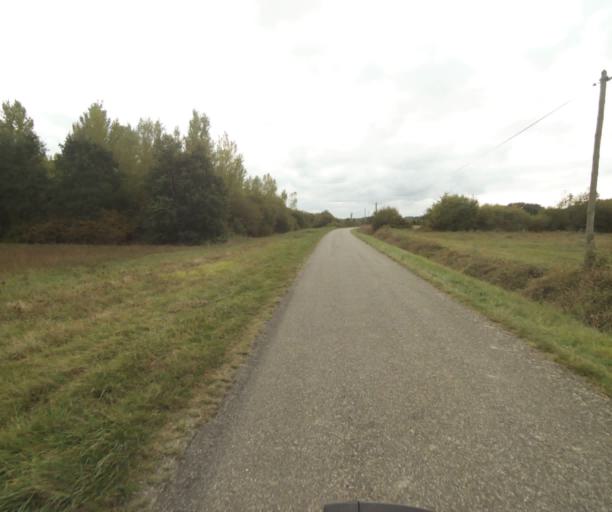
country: FR
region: Midi-Pyrenees
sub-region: Departement de la Haute-Garonne
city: Launac
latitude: 43.8376
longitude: 1.1059
